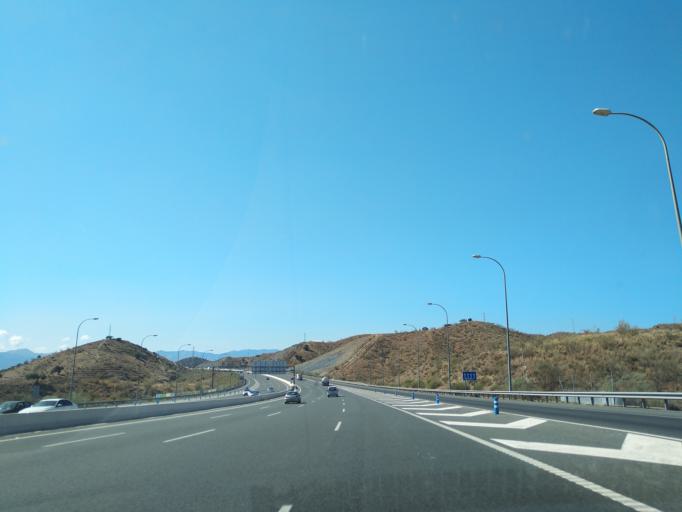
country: ES
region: Andalusia
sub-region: Provincia de Malaga
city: Malaga
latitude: 36.7501
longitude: -4.4960
